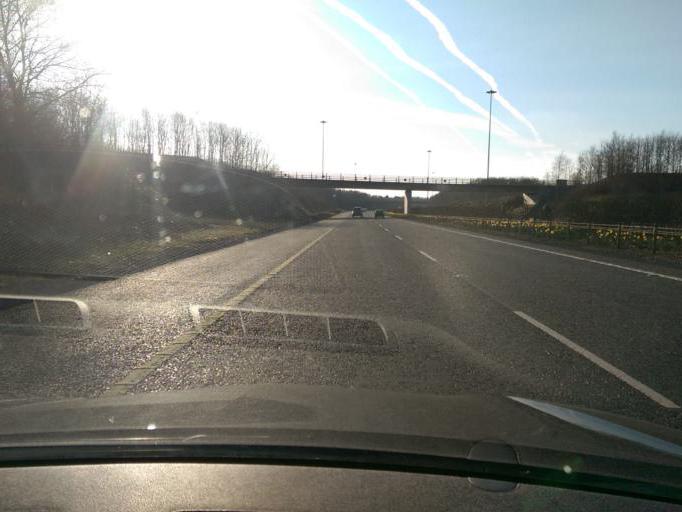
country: IE
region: Leinster
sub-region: Laois
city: Portlaoise
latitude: 53.0132
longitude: -7.3023
